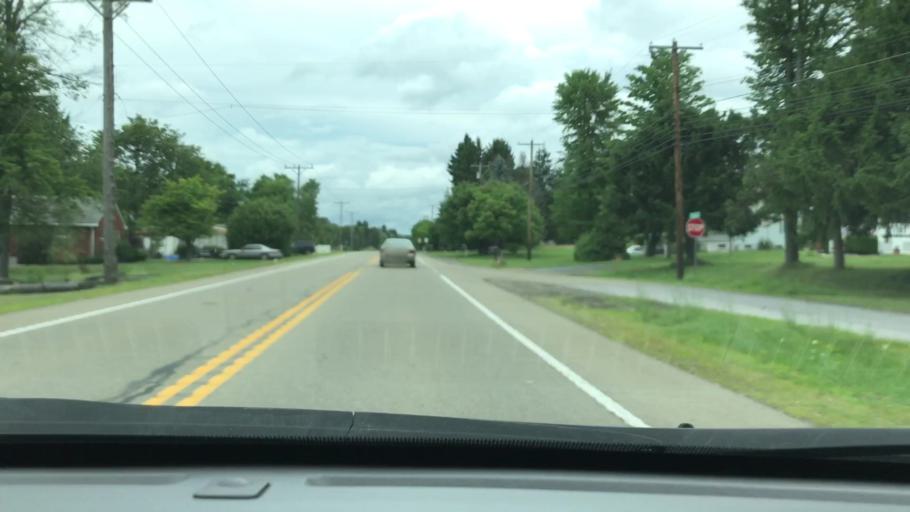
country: US
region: Pennsylvania
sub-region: Elk County
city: Johnsonburg
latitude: 41.5035
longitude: -78.6793
